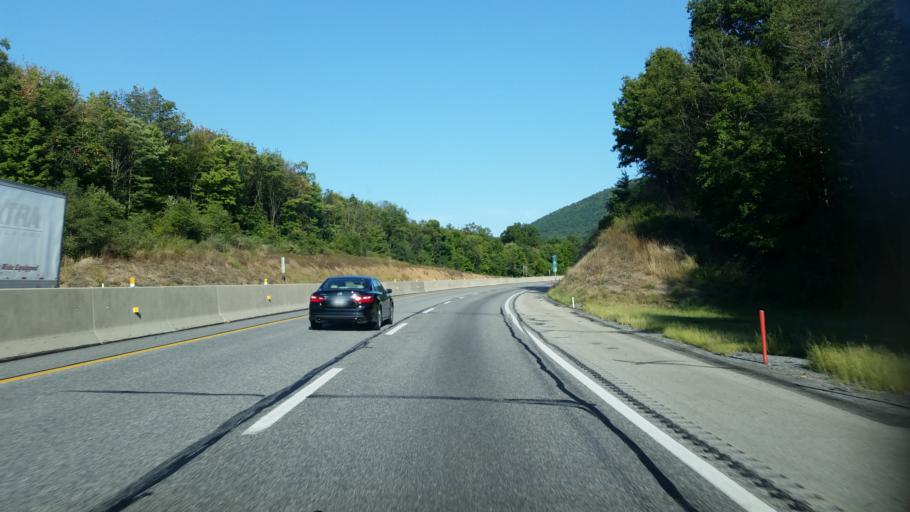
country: US
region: Pennsylvania
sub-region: Fulton County
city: McConnellsburg
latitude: 40.0687
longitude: -77.9316
